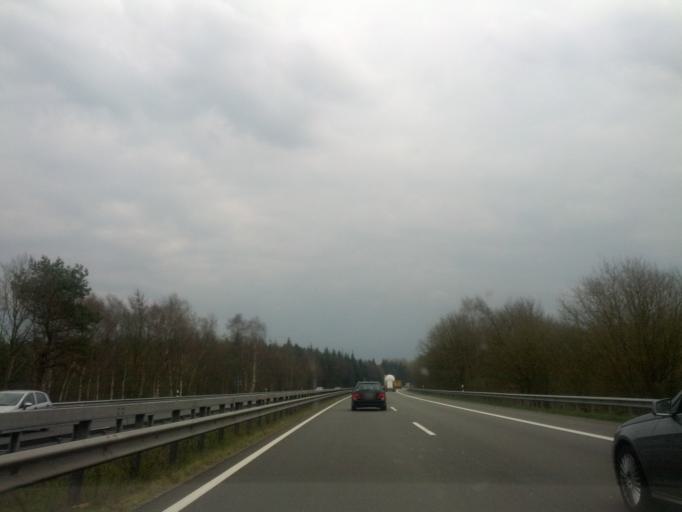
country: DE
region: Lower Saxony
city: Bad Zwischenahn
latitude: 53.2431
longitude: 8.0190
